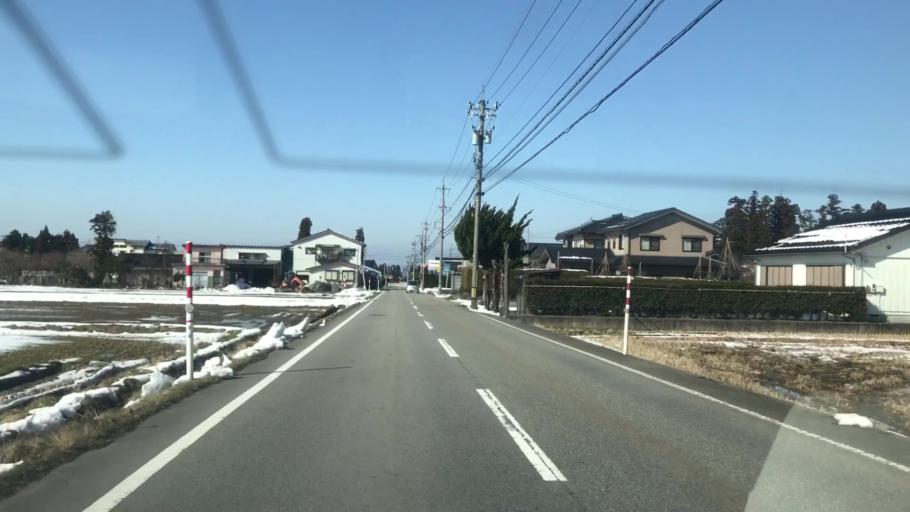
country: JP
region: Toyama
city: Toyama-shi
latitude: 36.6259
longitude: 137.2773
